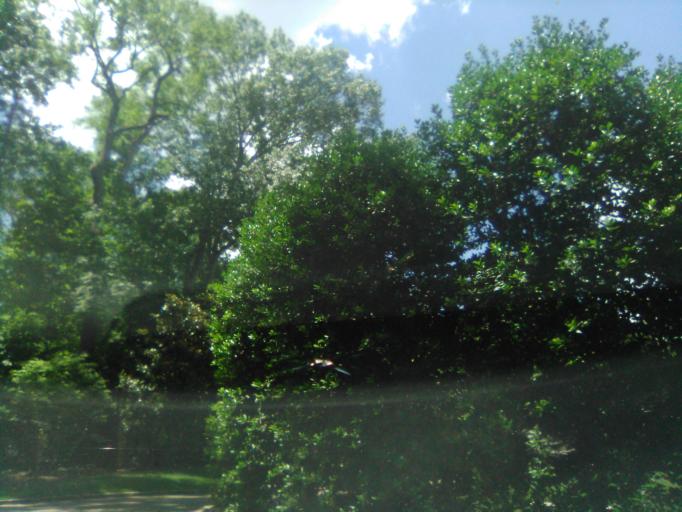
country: US
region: Tennessee
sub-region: Davidson County
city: Belle Meade
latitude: 36.1040
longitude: -86.8541
